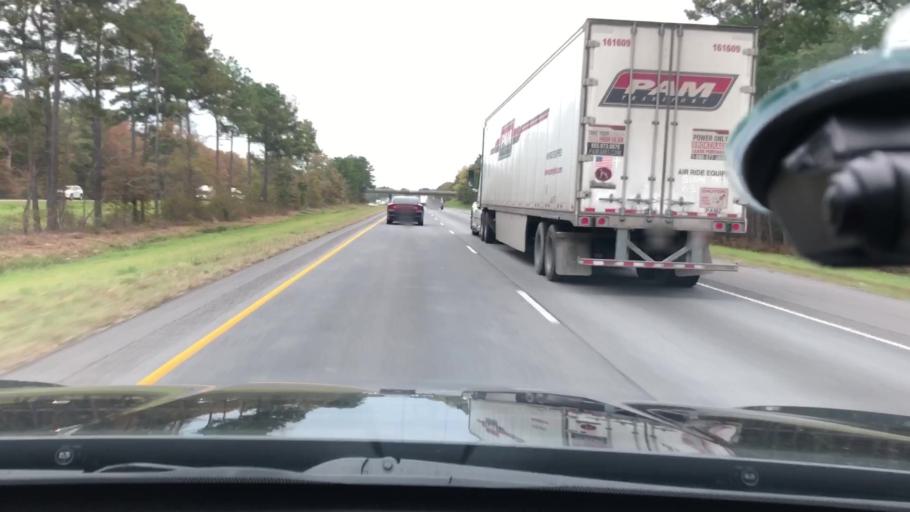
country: US
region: Arkansas
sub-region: Hempstead County
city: Hope
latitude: 33.6230
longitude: -93.7709
